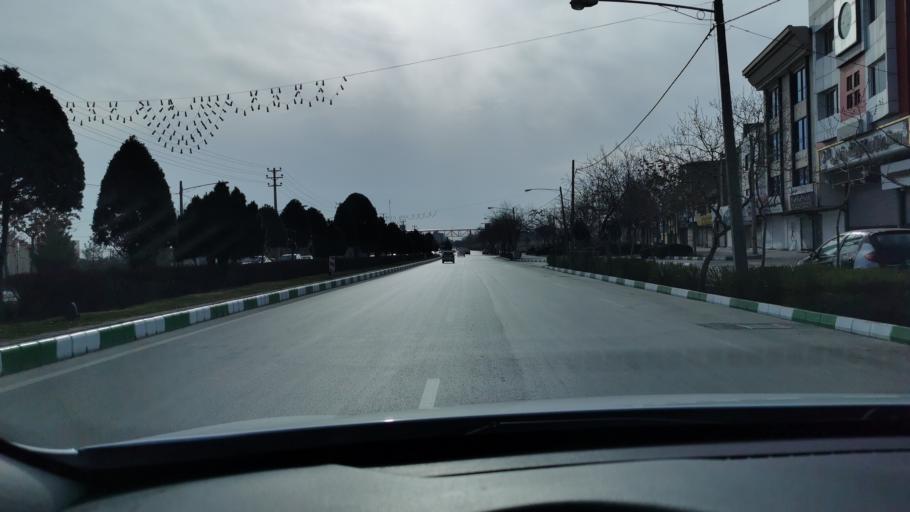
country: IR
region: Razavi Khorasan
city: Mashhad
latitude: 36.3025
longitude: 59.5170
